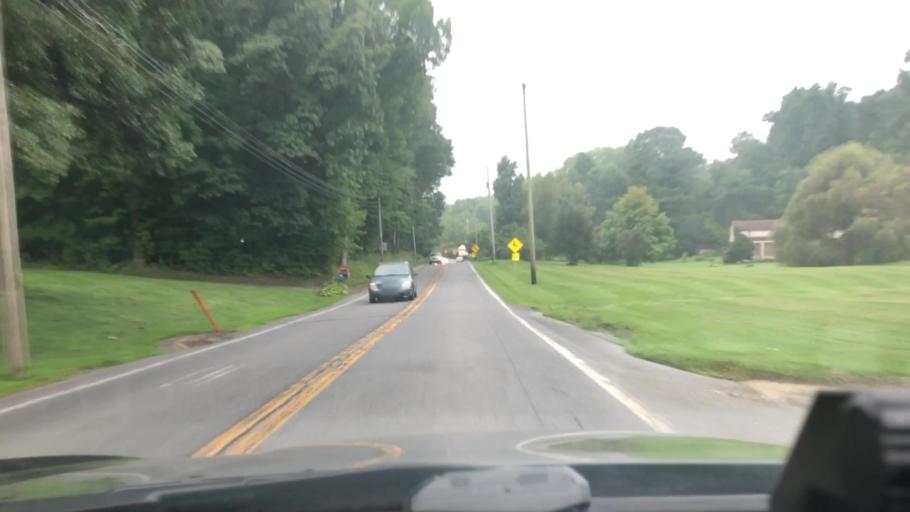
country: US
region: Pennsylvania
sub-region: Berks County
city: Kutztown
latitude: 40.5743
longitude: -75.8037
